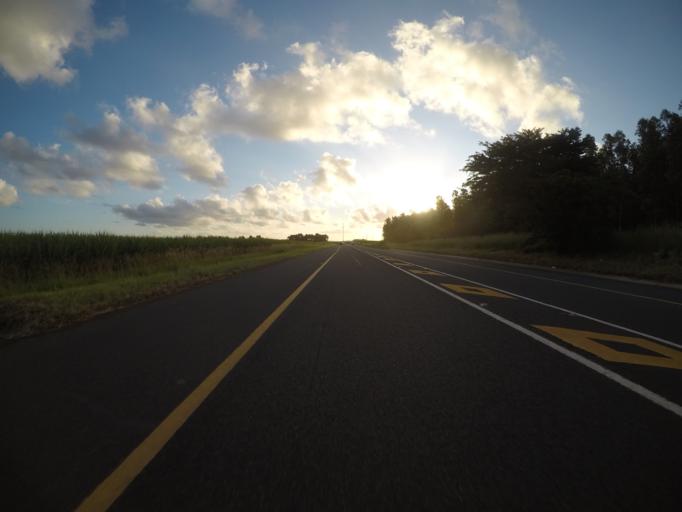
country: ZA
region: KwaZulu-Natal
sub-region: uThungulu District Municipality
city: Empangeni
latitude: -28.6999
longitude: 31.9729
